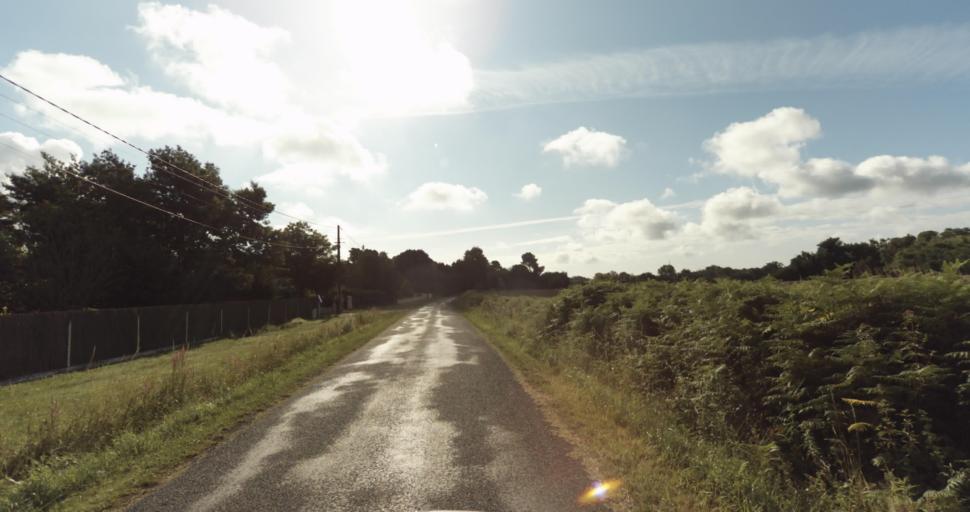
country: FR
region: Aquitaine
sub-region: Departement de la Gironde
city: Bazas
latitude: 44.4339
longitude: -0.2510
